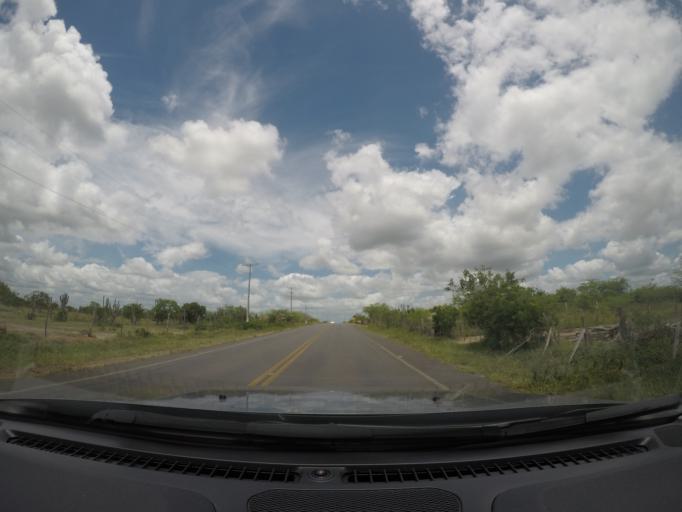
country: BR
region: Bahia
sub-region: Ipira
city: Ipira
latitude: -12.2998
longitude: -39.8918
